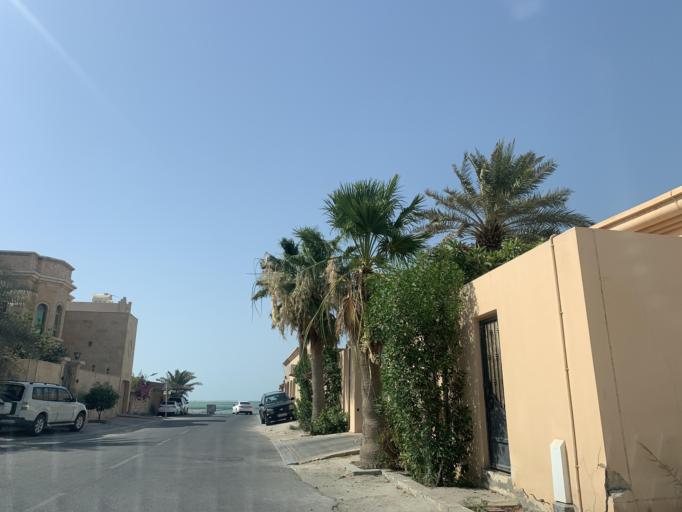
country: BH
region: Manama
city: Jidd Hafs
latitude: 26.2334
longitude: 50.4843
